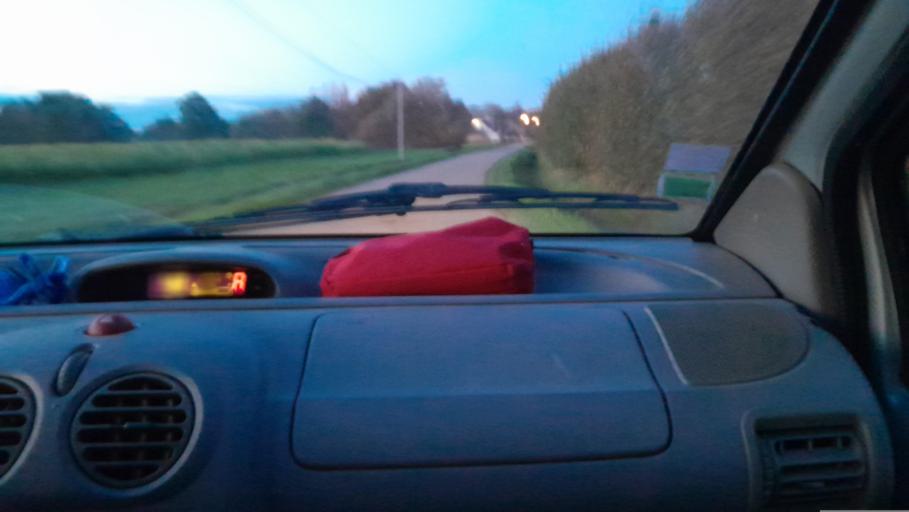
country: FR
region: Brittany
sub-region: Departement d'Ille-et-Vilaine
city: Rannee
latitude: 47.8818
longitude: -1.1803
